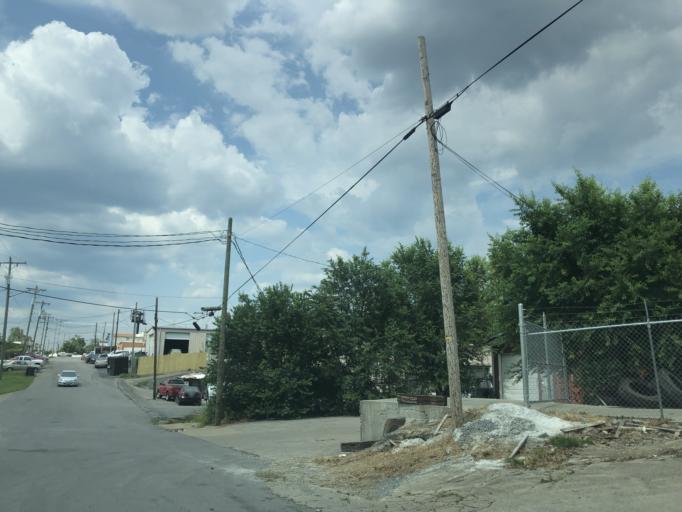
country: US
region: Tennessee
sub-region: Davidson County
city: Nashville
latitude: 36.1398
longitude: -86.7420
